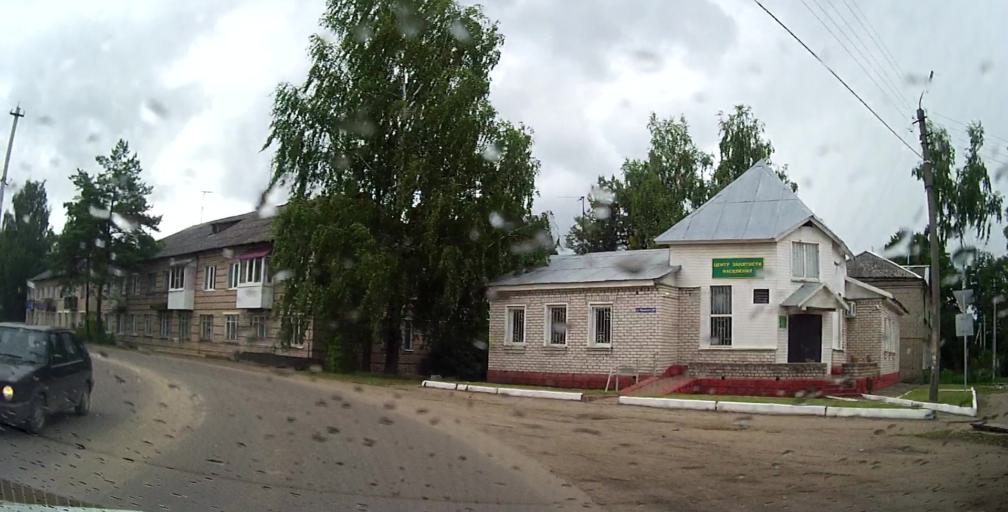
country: RU
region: Smolensk
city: Demidov
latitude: 55.2624
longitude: 31.5139
